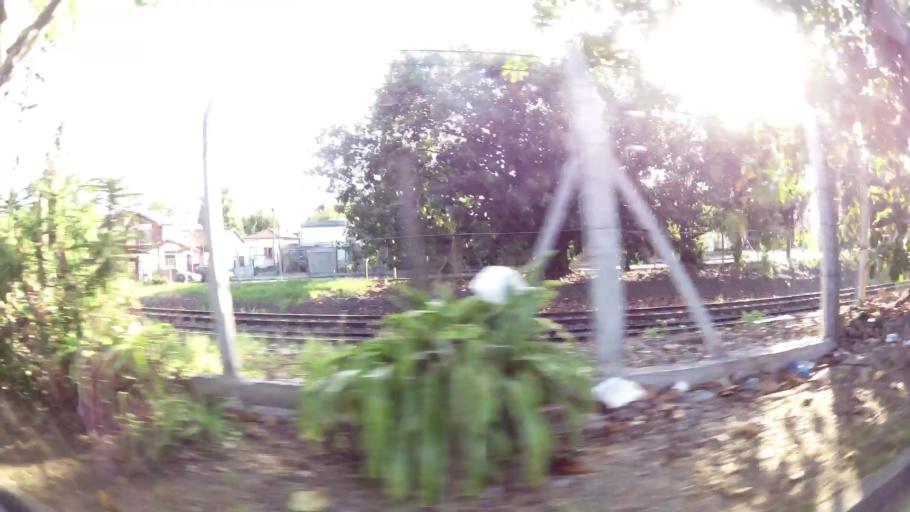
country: AR
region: Buenos Aires
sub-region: Partido de General San Martin
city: General San Martin
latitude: -34.5456
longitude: -58.5625
